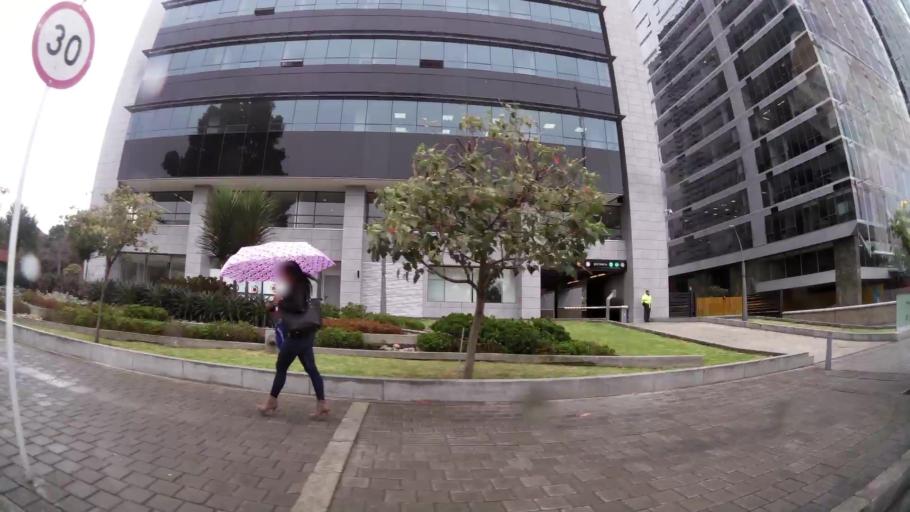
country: CO
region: Bogota D.C.
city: Bogota
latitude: 4.6594
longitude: -74.1054
